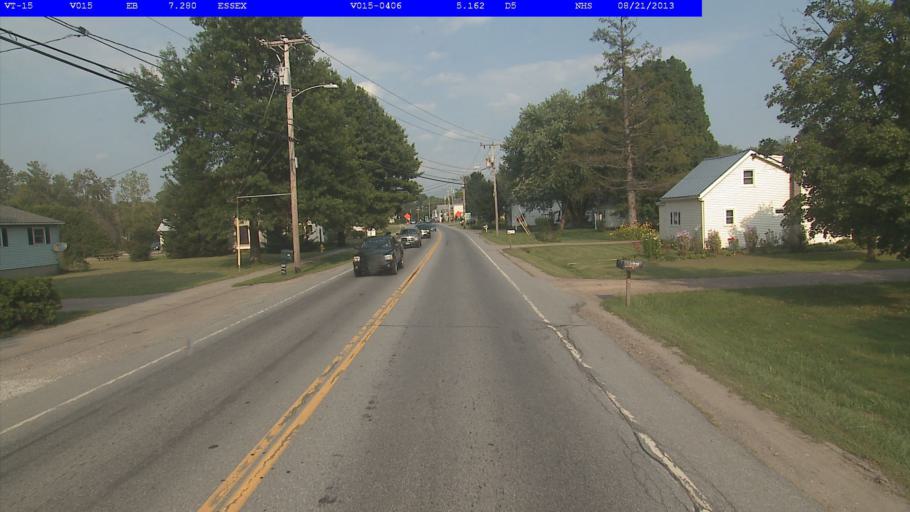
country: US
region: Vermont
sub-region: Chittenden County
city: Essex Junction
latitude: 44.5111
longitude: -73.0633
